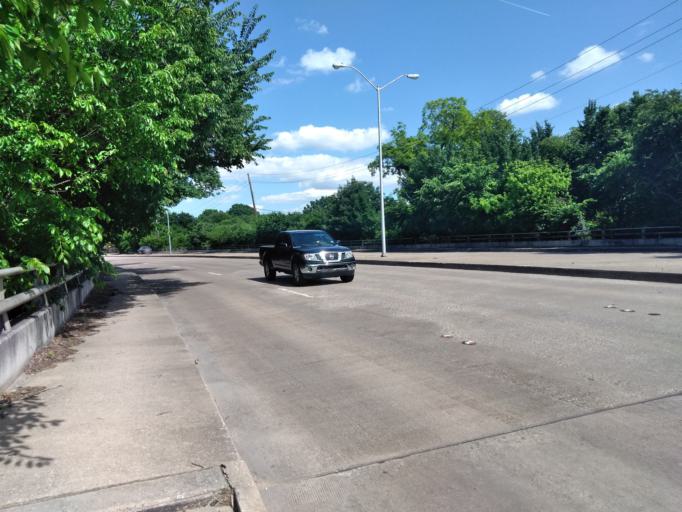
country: US
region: Texas
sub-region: Dallas County
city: Addison
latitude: 32.9984
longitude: -96.8148
